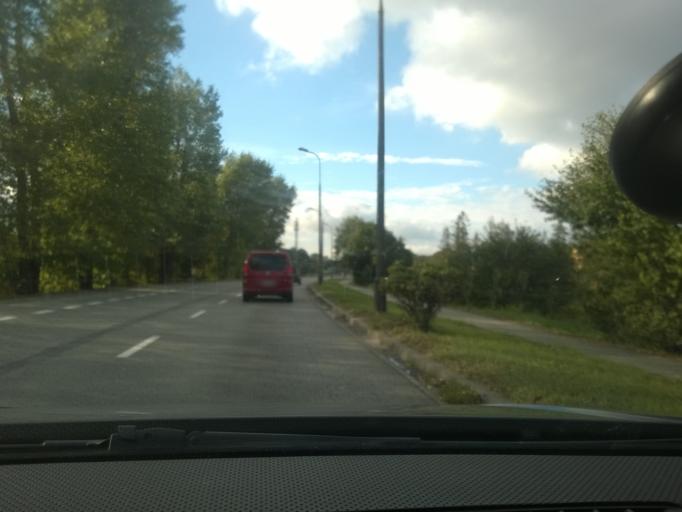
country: PL
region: Masovian Voivodeship
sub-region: Powiat pruszkowski
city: Pruszkow
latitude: 52.1776
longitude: 20.7883
